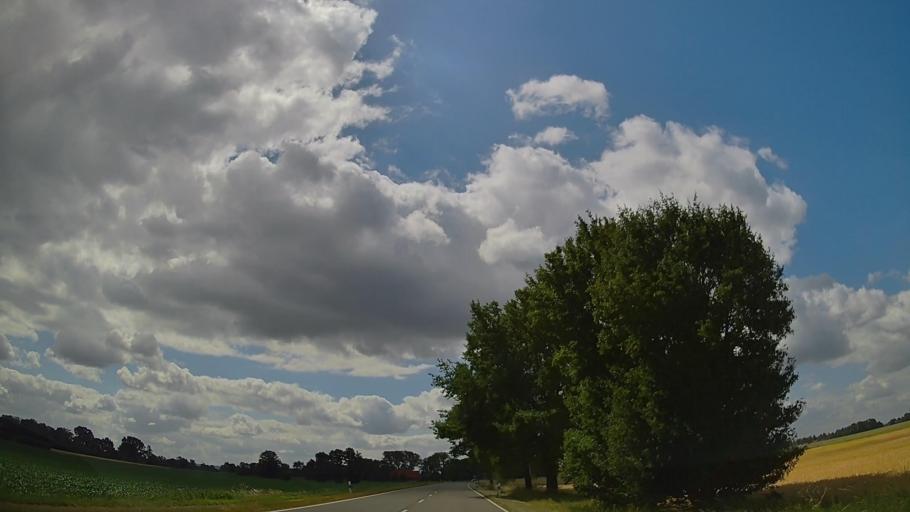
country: DE
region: Lower Saxony
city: Lembruch
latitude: 52.5403
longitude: 8.3752
